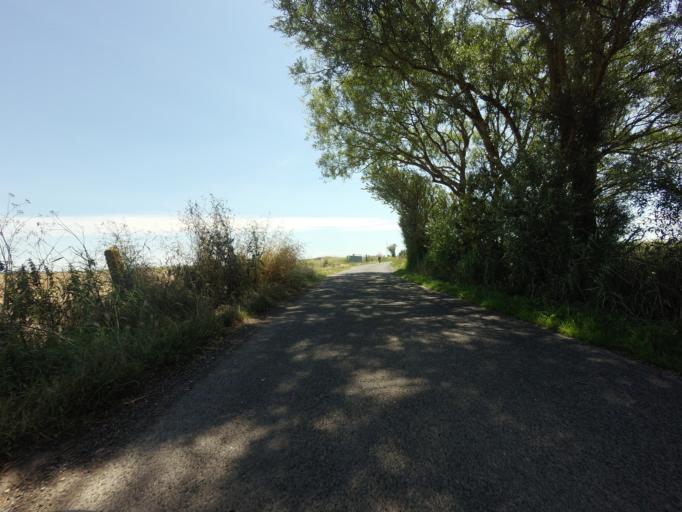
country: GB
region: England
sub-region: Kent
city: Lydd
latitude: 50.9822
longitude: 0.8952
